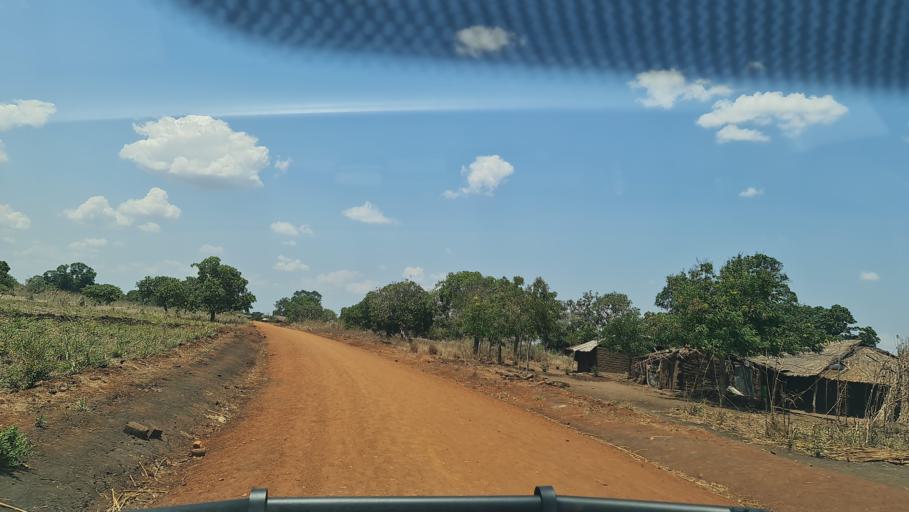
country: MZ
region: Nampula
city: Nacala
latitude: -14.8049
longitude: 40.0707
